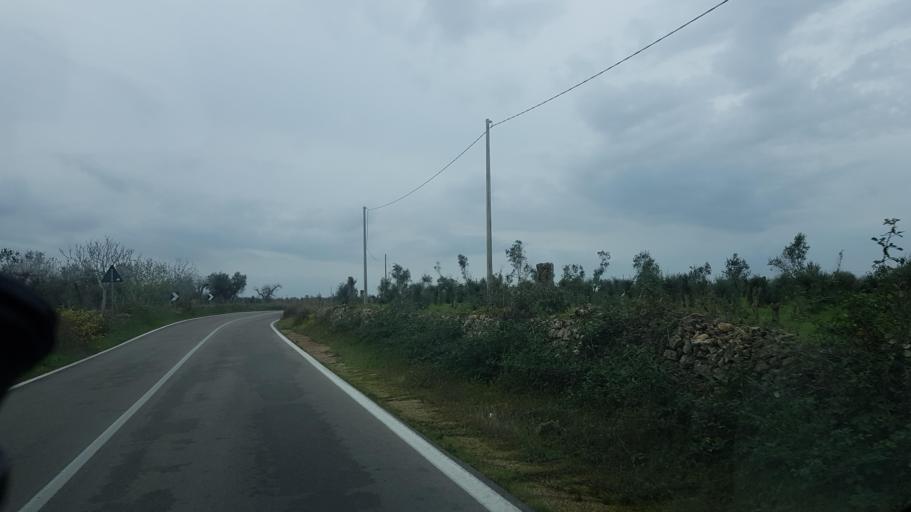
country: IT
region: Apulia
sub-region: Provincia di Lecce
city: Squinzano
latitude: 40.4571
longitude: 18.0539
